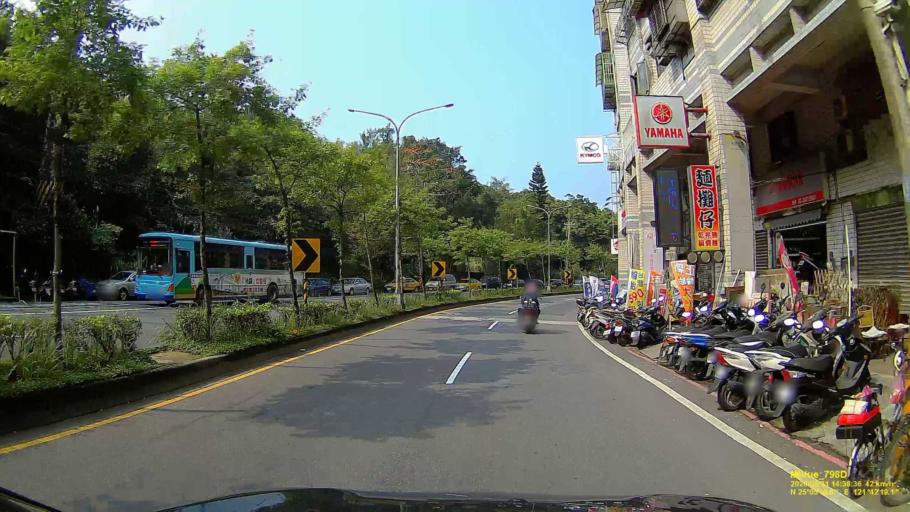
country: TW
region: Taiwan
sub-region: Keelung
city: Keelung
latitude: 25.0889
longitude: 121.7053
